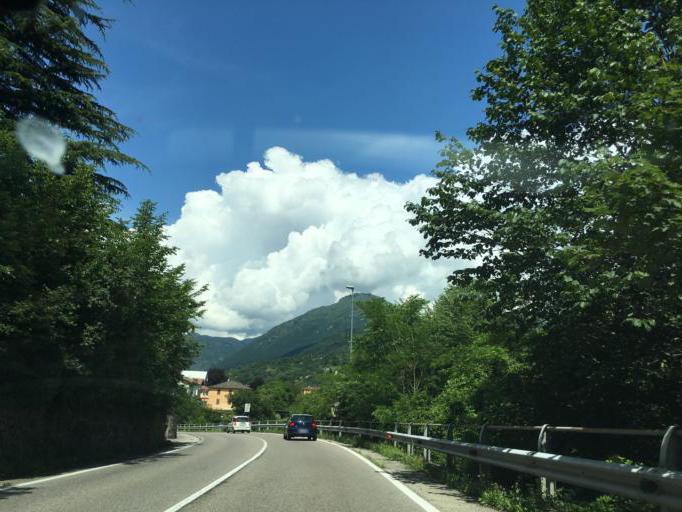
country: IT
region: Lombardy
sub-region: Provincia di Como
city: Grandola ed Uniti
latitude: 46.0218
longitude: 9.2163
